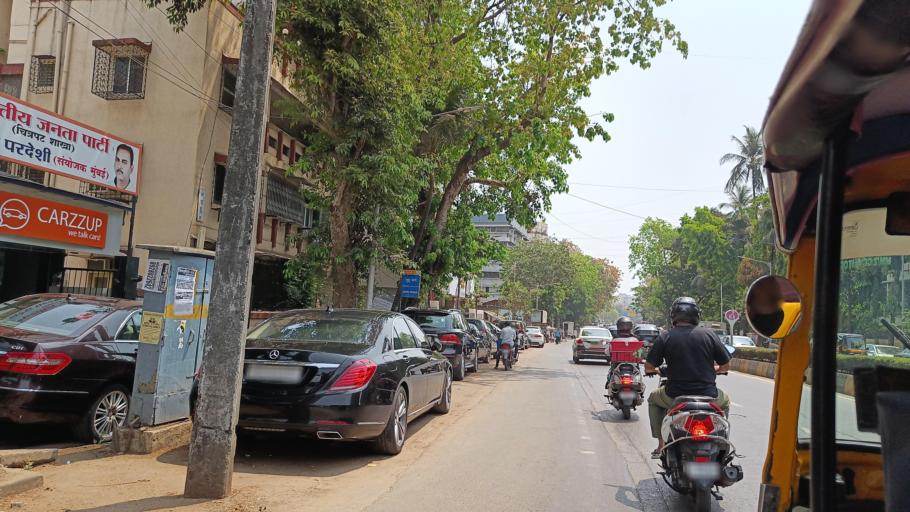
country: IN
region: Maharashtra
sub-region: Mumbai Suburban
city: Mumbai
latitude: 19.0861
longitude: 72.8274
